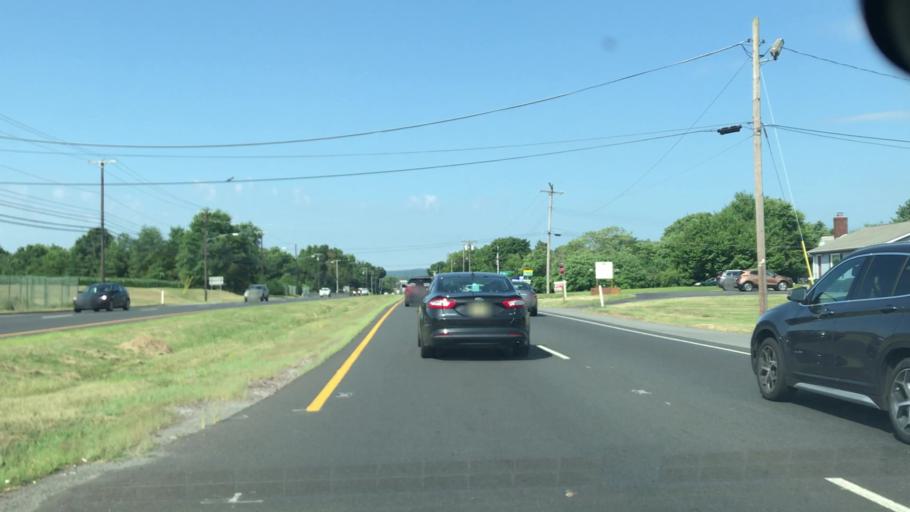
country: US
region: New Jersey
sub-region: Hunterdon County
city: Flemington
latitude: 40.5127
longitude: -74.8287
